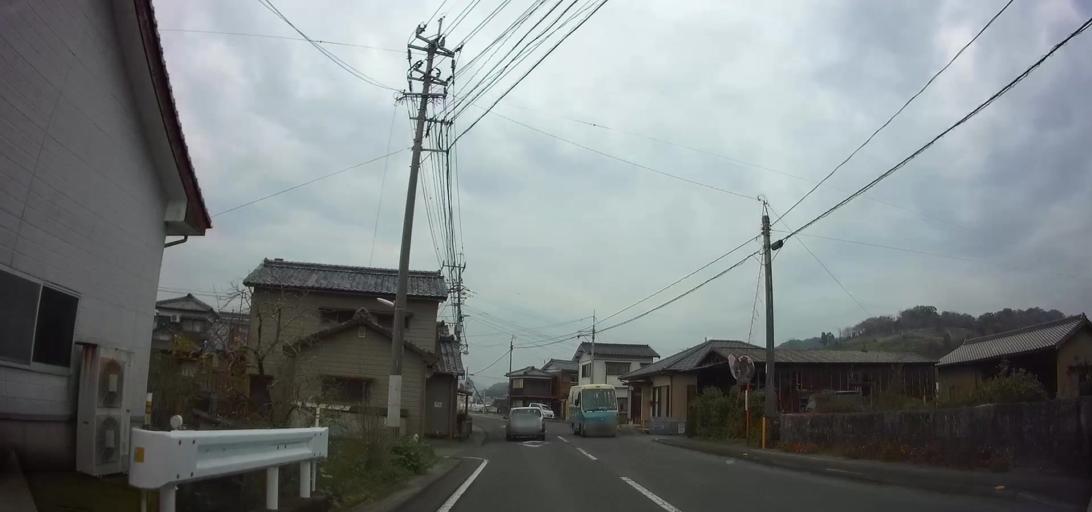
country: JP
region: Nagasaki
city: Shimabara
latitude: 32.6563
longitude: 130.2572
